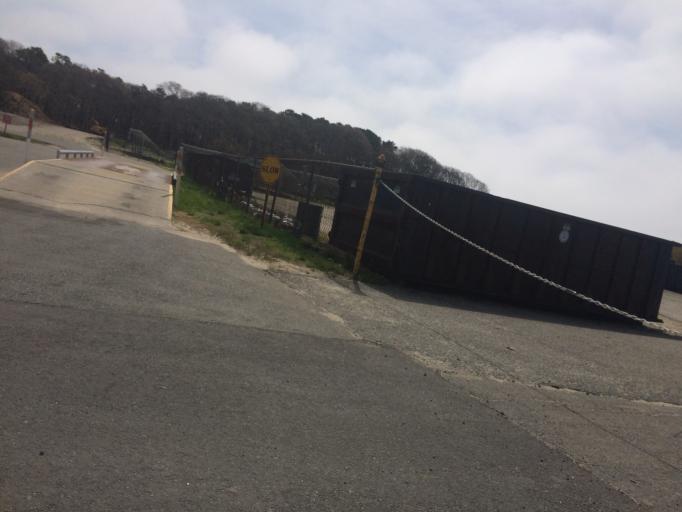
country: US
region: Massachusetts
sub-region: Barnstable County
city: Provincetown
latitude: 42.0601
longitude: -70.1951
